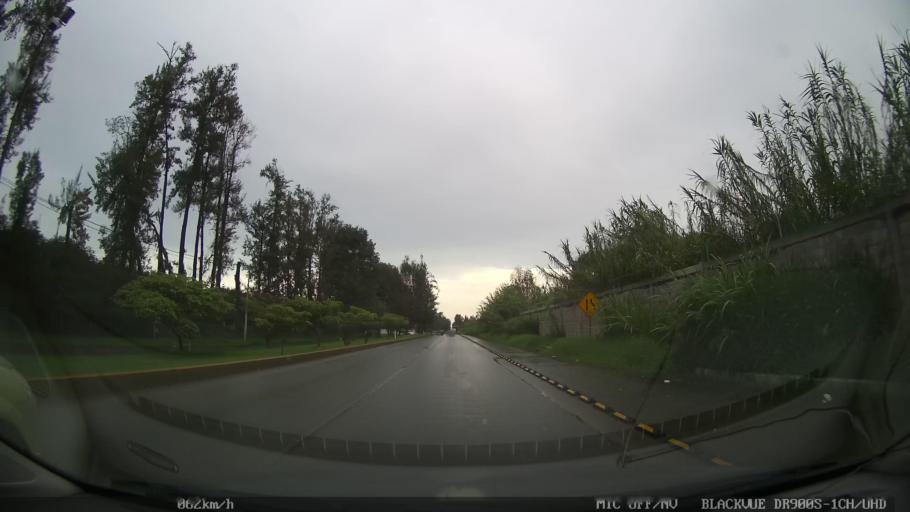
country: MX
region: Michoacan
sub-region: Uruapan
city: Santa Rosa (Santa Barbara)
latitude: 19.4019
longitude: -102.0324
